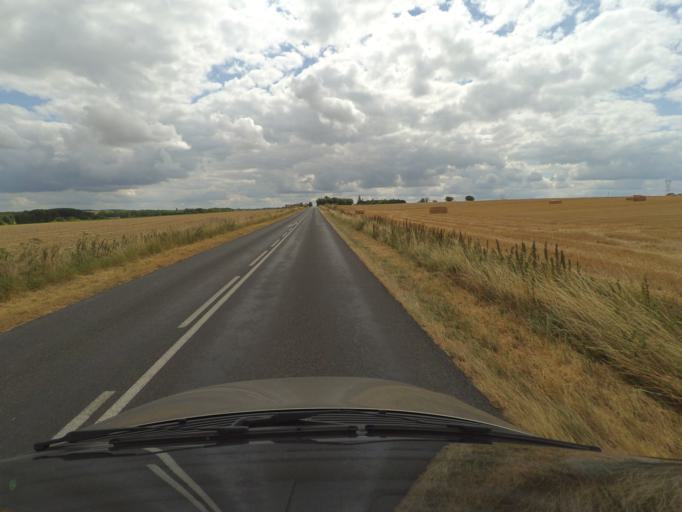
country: FR
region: Poitou-Charentes
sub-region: Departement de la Vienne
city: Saint-Gervais-les-Trois-Clochers
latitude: 46.9626
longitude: 0.3852
